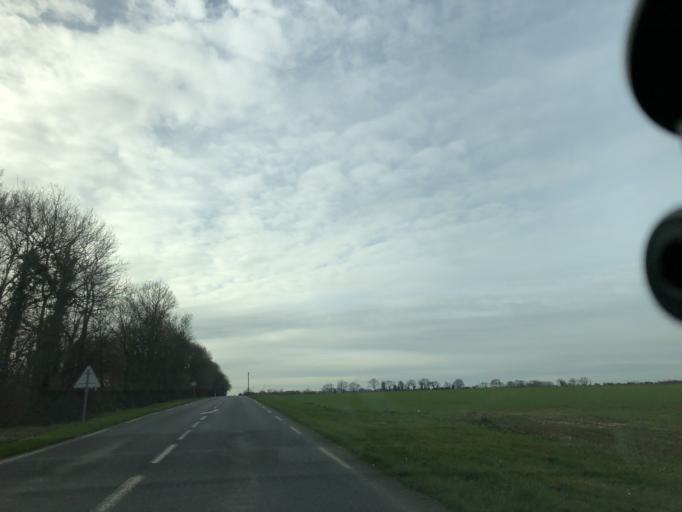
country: FR
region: Lower Normandy
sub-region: Departement du Calvados
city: Hermanville-sur-Mer
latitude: 49.2881
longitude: -0.3207
